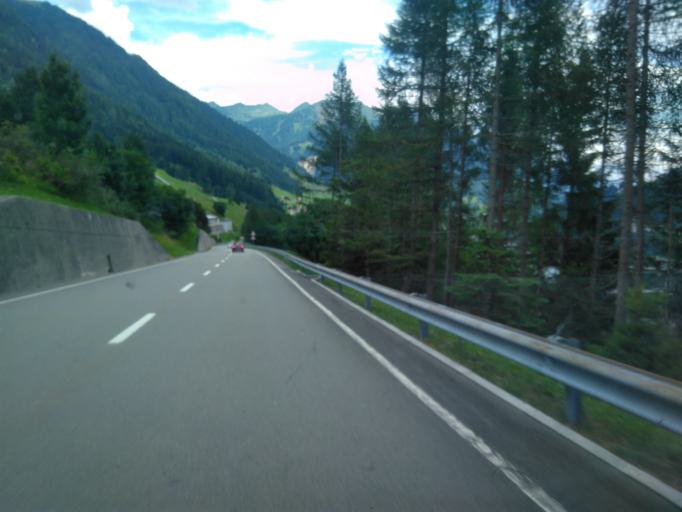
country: CH
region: Ticino
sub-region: Leventina District
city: Airolo
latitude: 46.5276
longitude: 8.5923
